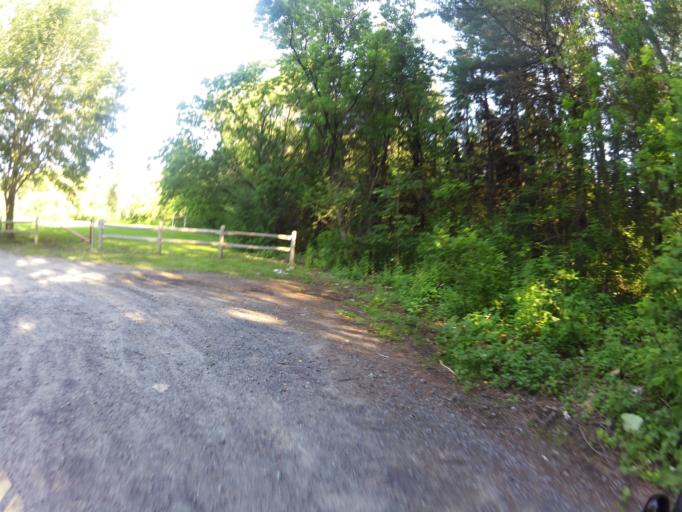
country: CA
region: Ontario
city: Bells Corners
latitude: 45.3148
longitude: -75.7324
